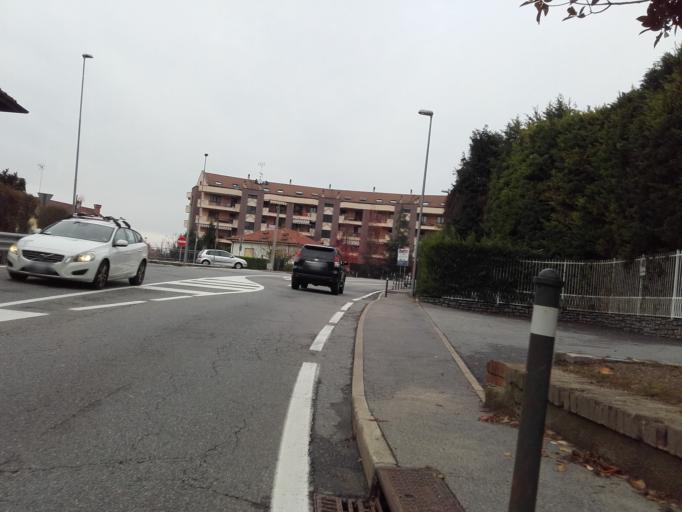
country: IT
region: Piedmont
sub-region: Provincia di Torino
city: San Mauro Torinese
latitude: 45.1109
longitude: 7.7760
